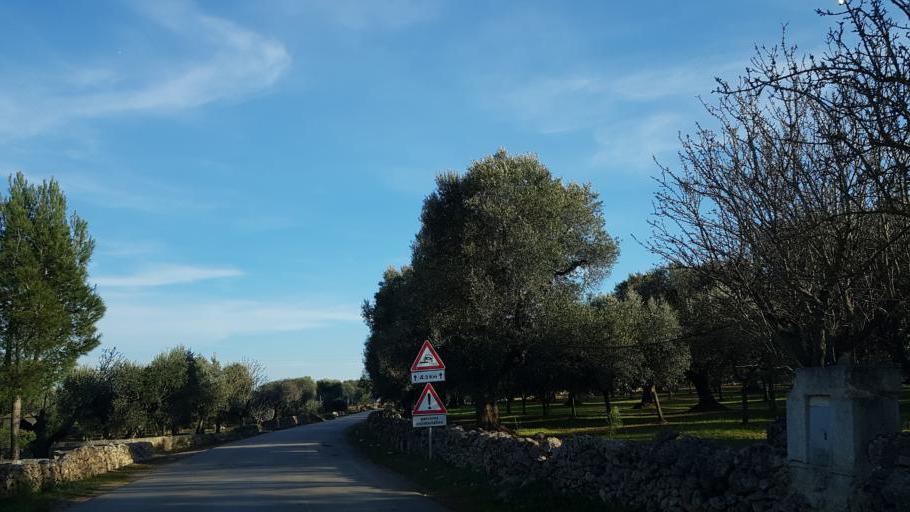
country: IT
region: Apulia
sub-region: Provincia di Brindisi
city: San Vito dei Normanni
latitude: 40.7035
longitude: 17.7239
